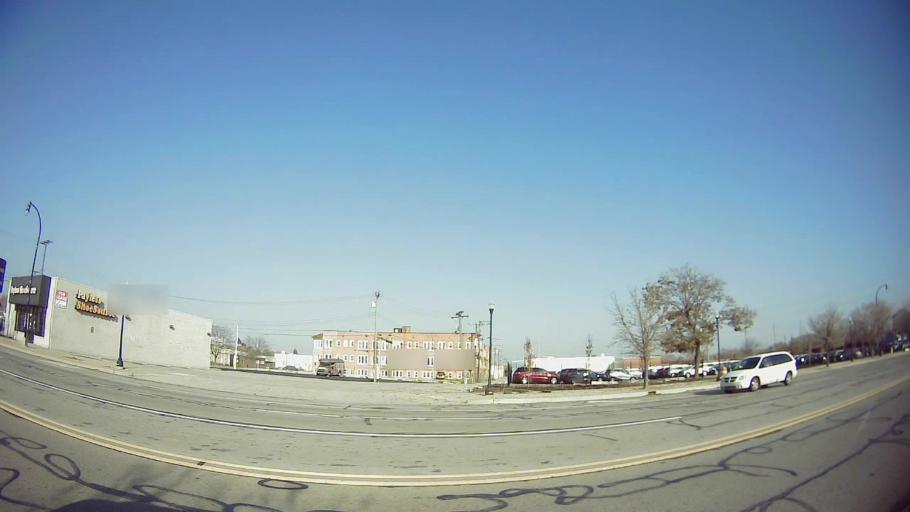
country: US
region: Michigan
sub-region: Wayne County
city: Dearborn
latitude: 42.3242
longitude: -83.1679
